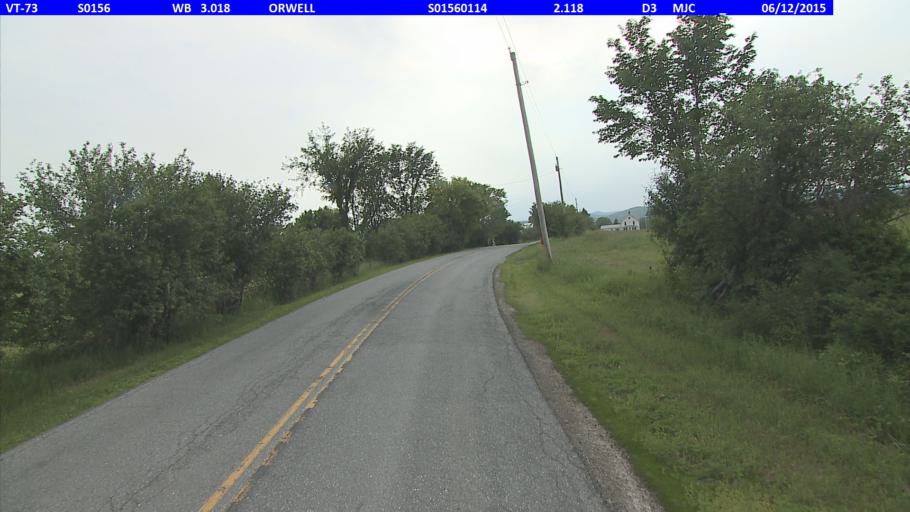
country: US
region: New York
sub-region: Essex County
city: Ticonderoga
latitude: 43.8300
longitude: -73.3308
